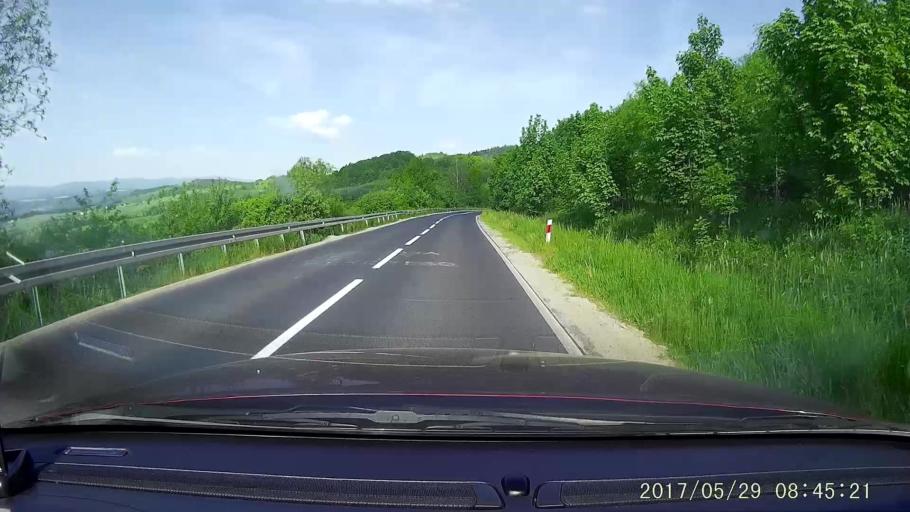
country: PL
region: Lower Silesian Voivodeship
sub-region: Powiat jeleniogorski
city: Jezow Sudecki
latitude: 50.9511
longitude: 15.8135
